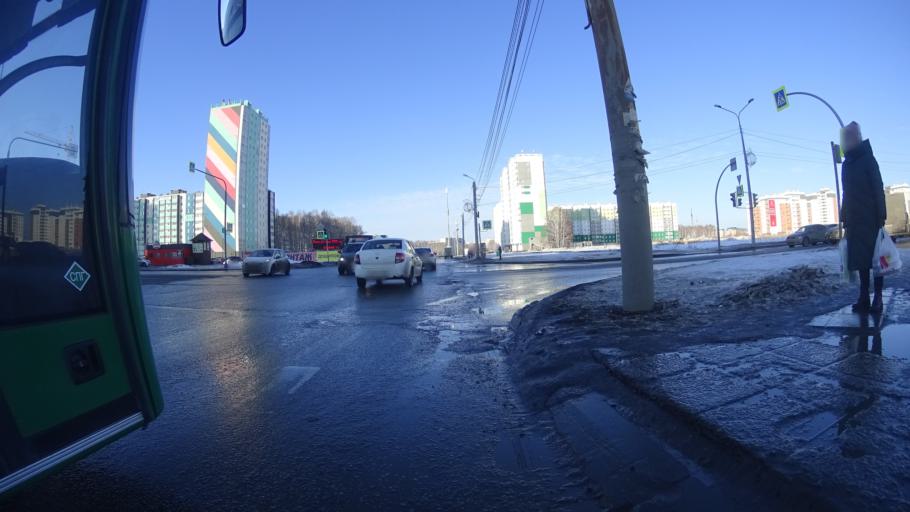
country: RU
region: Chelyabinsk
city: Roshchino
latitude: 55.2098
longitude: 61.2844
